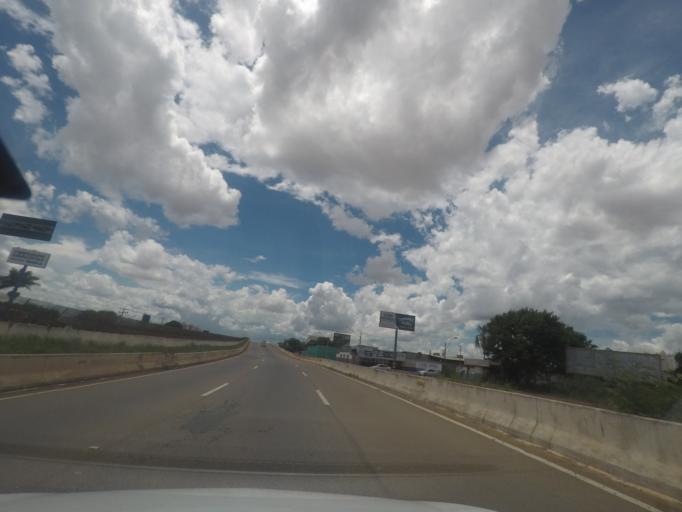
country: BR
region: Goias
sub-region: Goiania
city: Goiania
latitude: -16.7017
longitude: -49.3359
